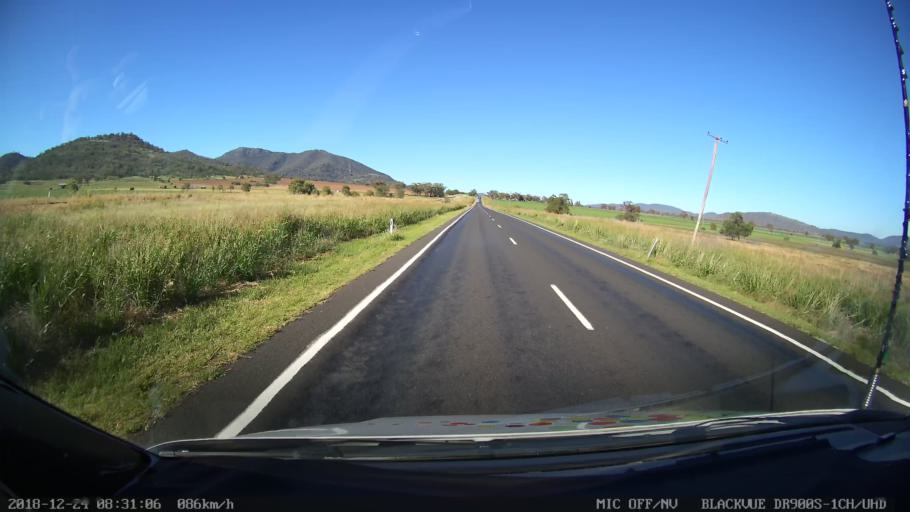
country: AU
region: New South Wales
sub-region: Tamworth Municipality
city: Phillip
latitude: -31.2715
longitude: 150.7160
